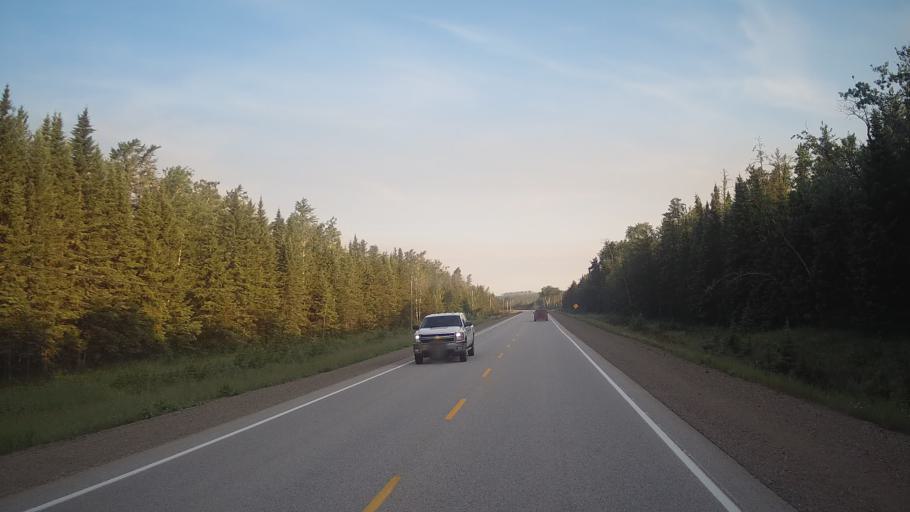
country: CA
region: Ontario
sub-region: Rainy River District
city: Atikokan
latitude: 49.2480
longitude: -91.0991
